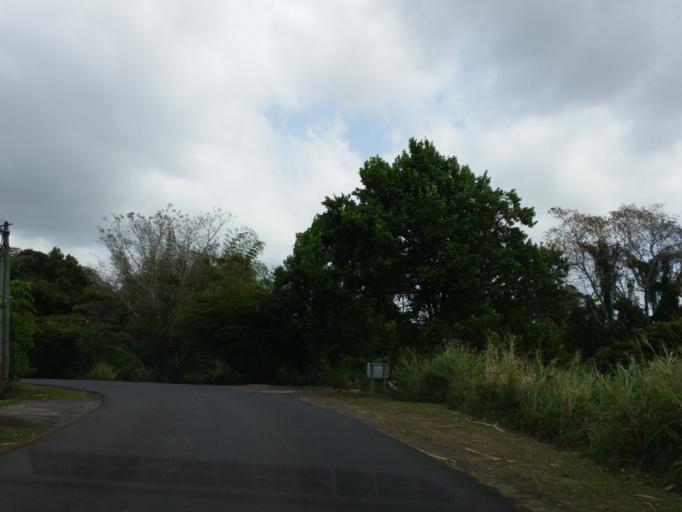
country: RE
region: Reunion
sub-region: Reunion
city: Sainte-Suzanne
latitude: -20.9165
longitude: 55.6179
